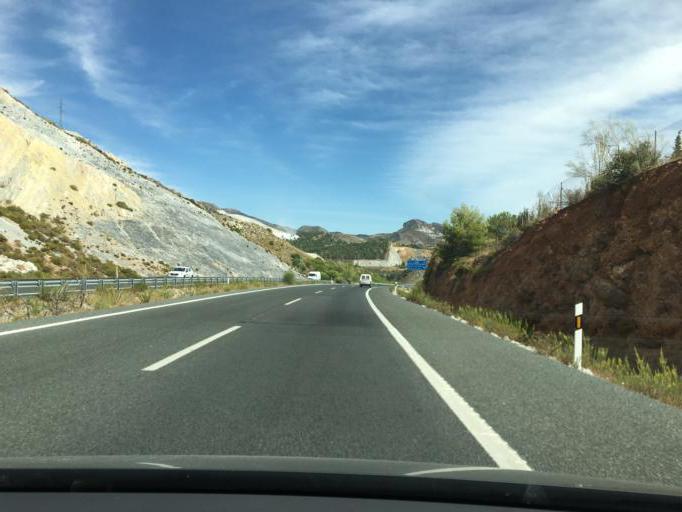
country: ES
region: Andalusia
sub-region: Provincia de Granada
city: Huetor Santillan
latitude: 37.2276
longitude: -3.5119
